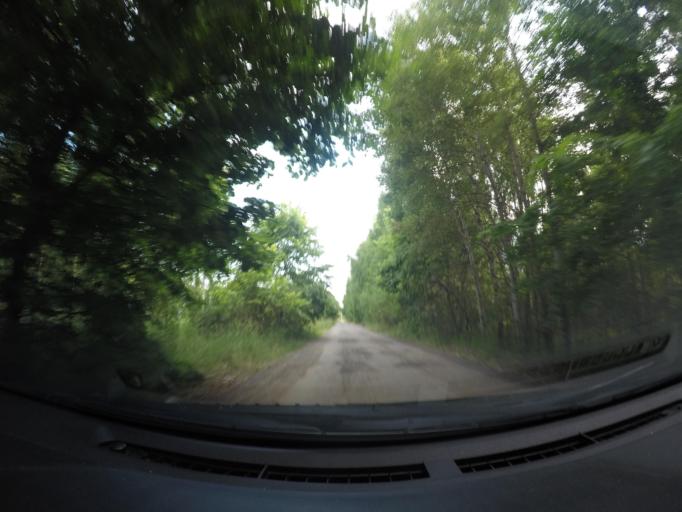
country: RU
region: Moskovskaya
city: Krasnyy Tkach
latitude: 55.4230
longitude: 39.2382
